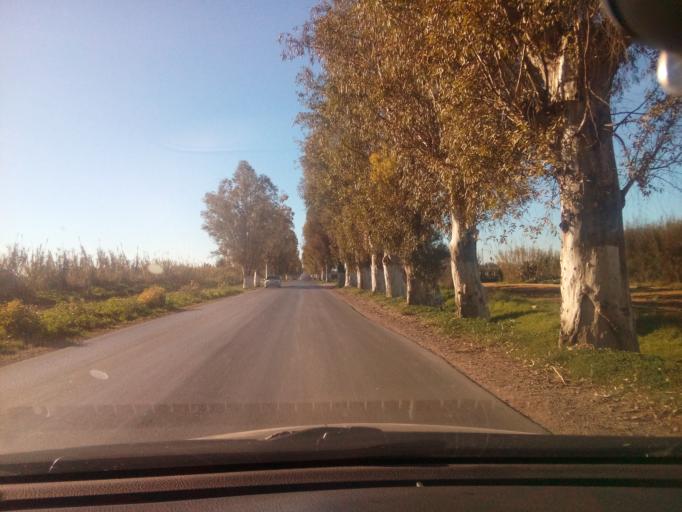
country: DZ
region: Mostaganem
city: Mostaganem
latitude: 35.9047
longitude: 0.2018
